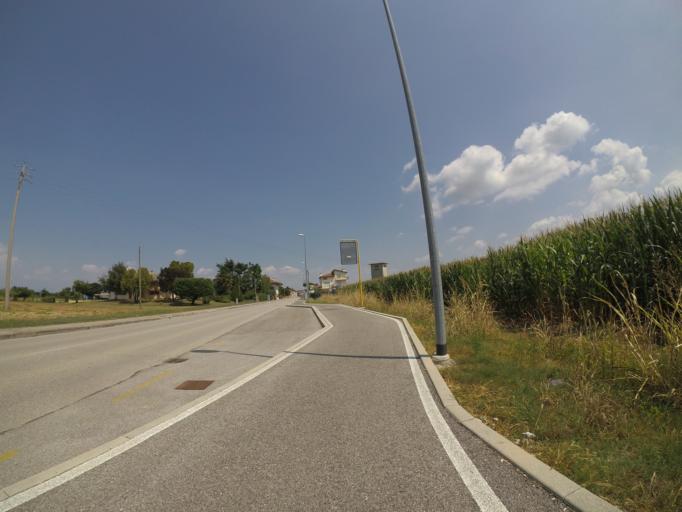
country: IT
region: Friuli Venezia Giulia
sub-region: Provincia di Udine
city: Sedegliano
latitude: 46.0085
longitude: 12.9692
